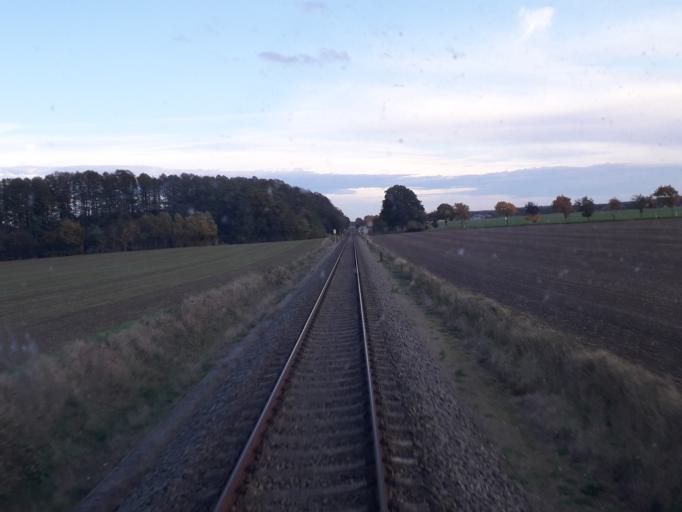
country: DE
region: Brandenburg
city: Wittstock
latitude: 53.1320
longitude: 12.5061
